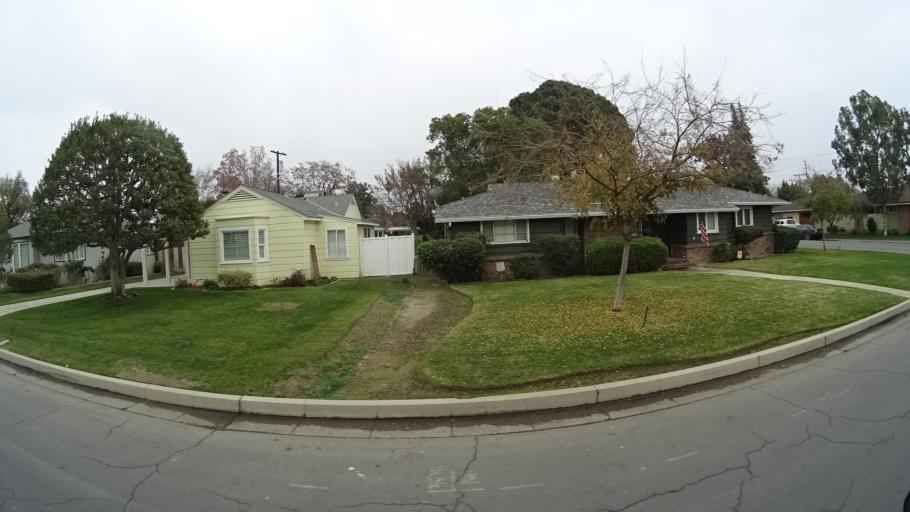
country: US
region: California
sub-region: Kern County
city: Bakersfield
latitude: 35.3834
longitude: -119.0288
